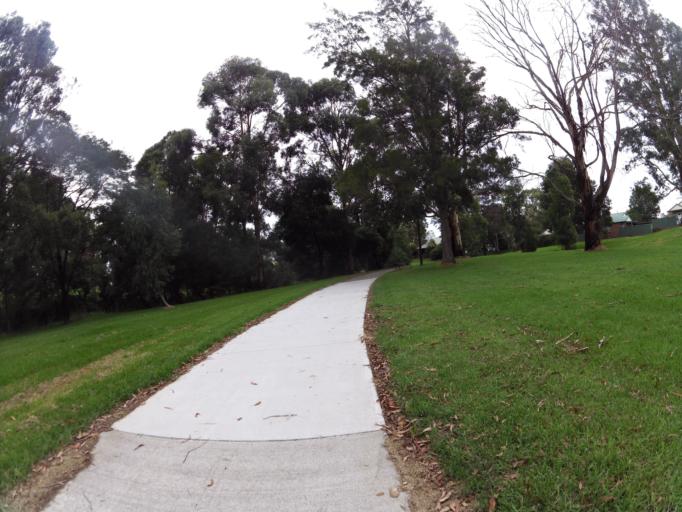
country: AU
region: Victoria
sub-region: Latrobe
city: Traralgon
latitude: -38.1992
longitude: 146.5414
